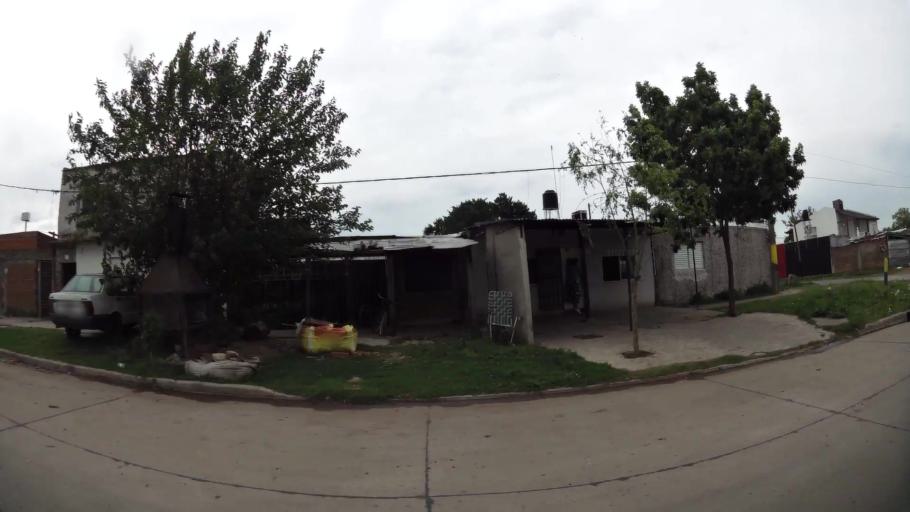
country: AR
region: Santa Fe
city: Gobernador Galvez
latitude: -33.0149
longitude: -60.6594
